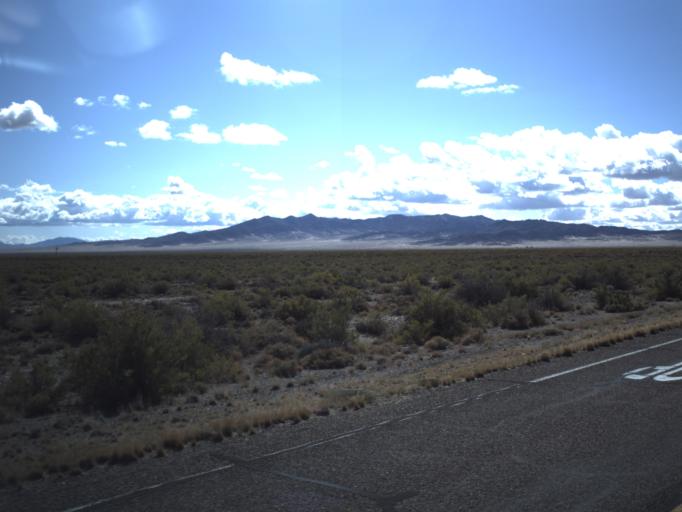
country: US
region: Nevada
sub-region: White Pine County
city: McGill
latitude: 39.0535
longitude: -114.0365
